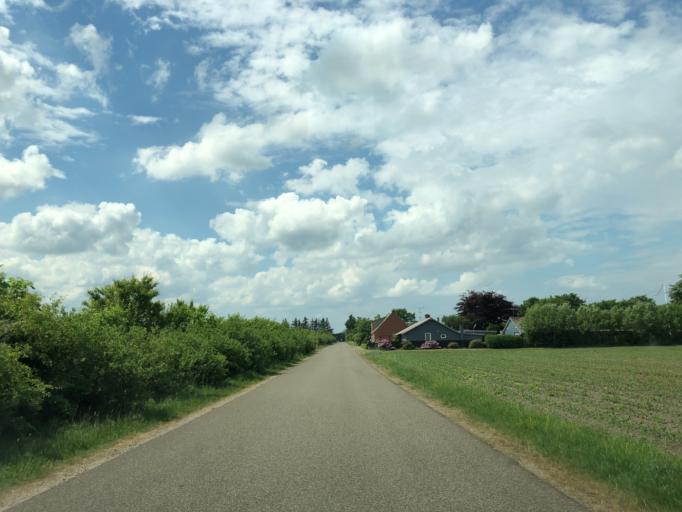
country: DK
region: Central Jutland
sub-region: Holstebro Kommune
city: Ulfborg
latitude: 56.3482
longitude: 8.3313
